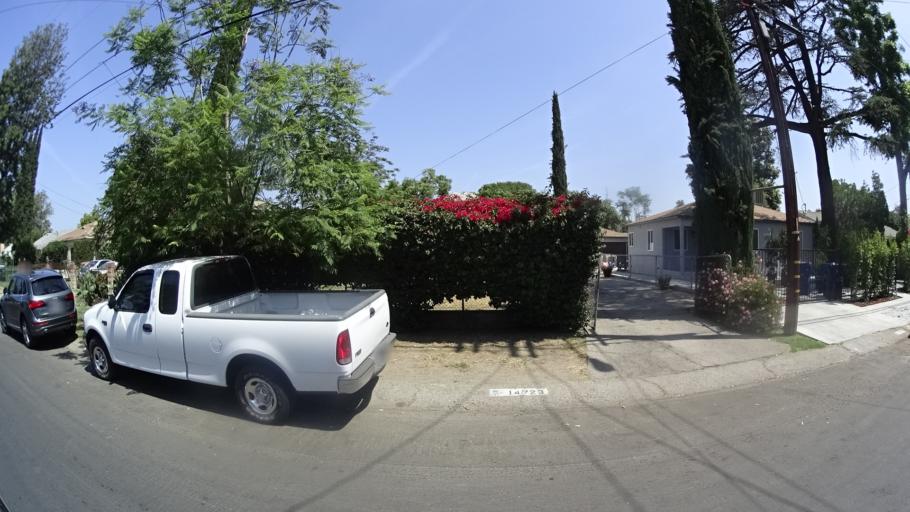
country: US
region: California
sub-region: Los Angeles County
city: Van Nuys
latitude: 34.2057
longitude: -118.4540
